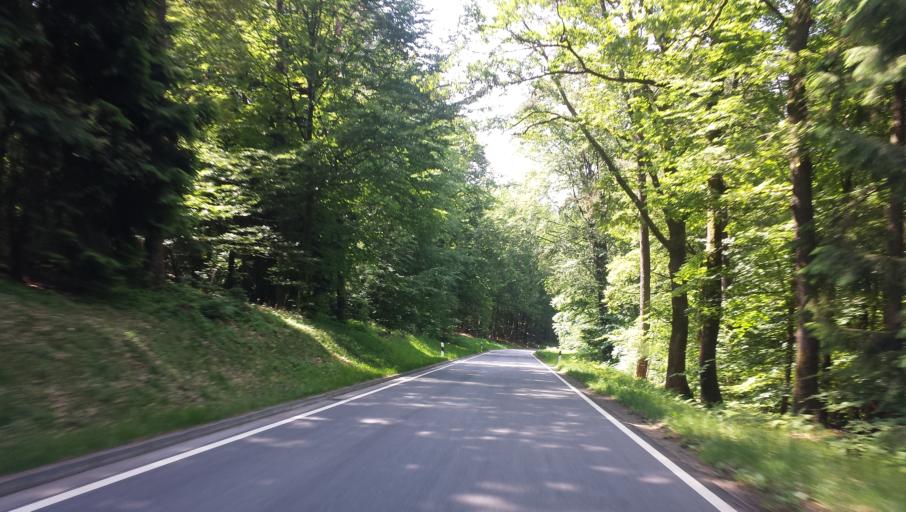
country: DE
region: Hesse
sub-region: Regierungsbezirk Darmstadt
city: Beerfelden
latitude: 49.5473
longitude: 8.9455
